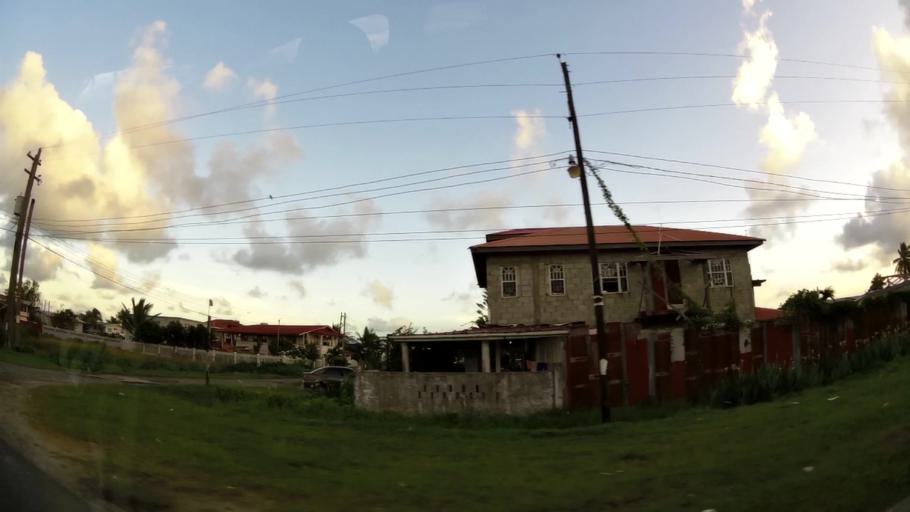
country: GY
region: Demerara-Mahaica
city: Georgetown
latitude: 6.8139
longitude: -58.1006
